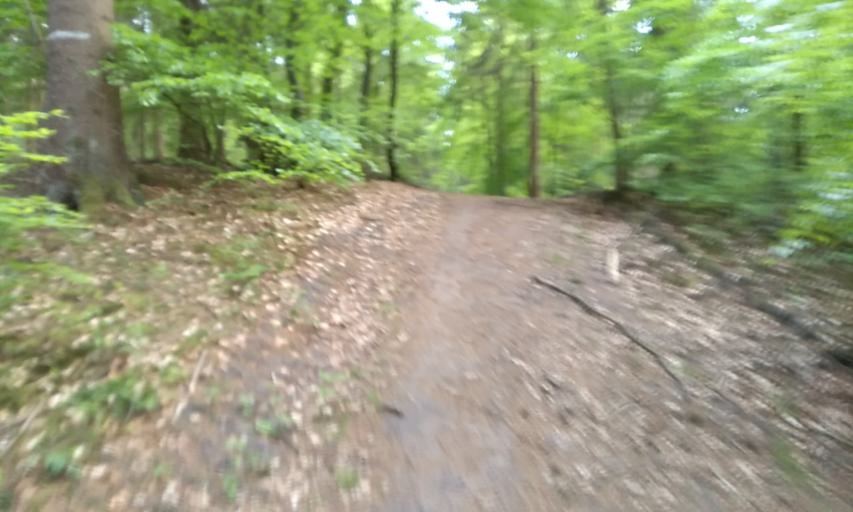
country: DE
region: Lower Saxony
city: Buxtehude
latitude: 53.4732
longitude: 9.6512
